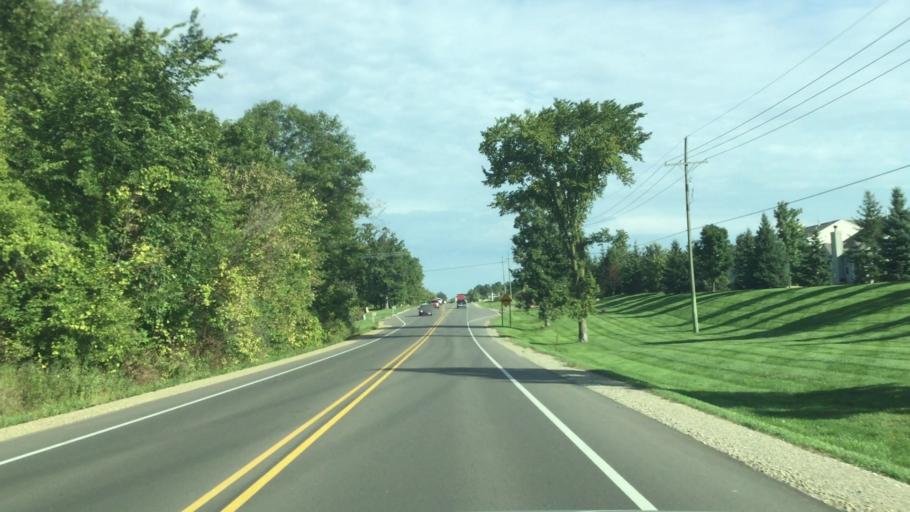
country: US
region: Michigan
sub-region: Livingston County
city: Howell
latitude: 42.6206
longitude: -83.8752
